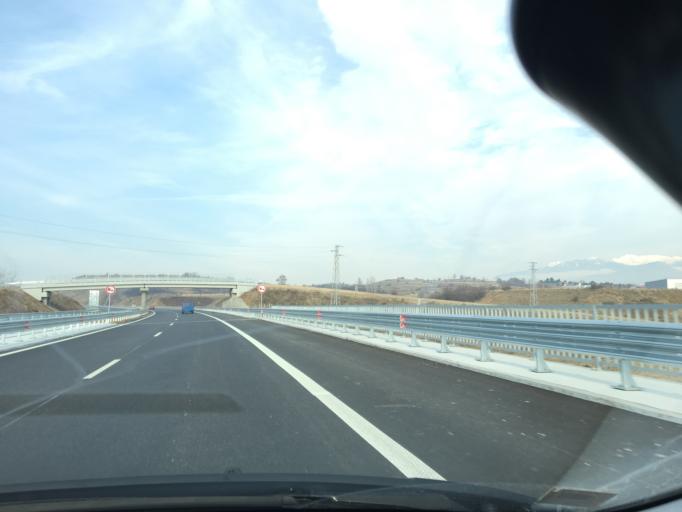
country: BG
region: Blagoevgrad
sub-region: Obshtina Sandanski
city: Sandanski
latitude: 41.5217
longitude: 23.2707
